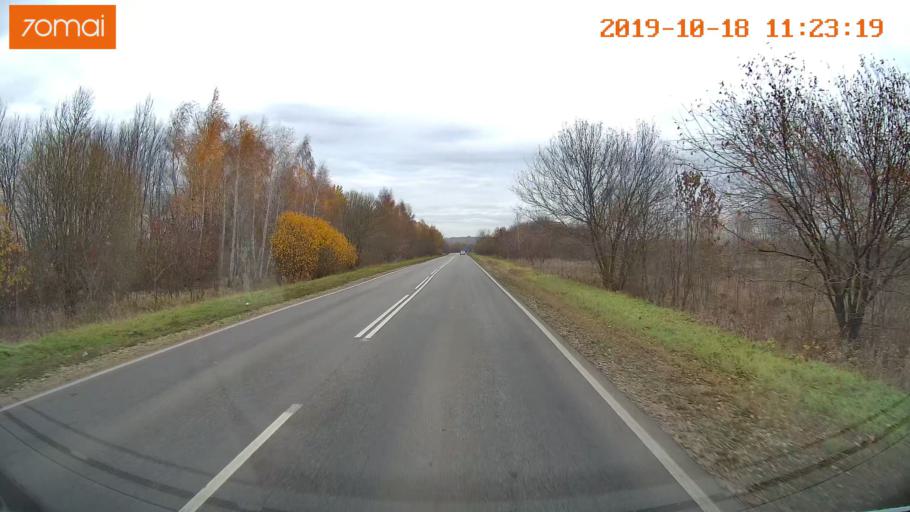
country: RU
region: Tula
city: Kimovsk
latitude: 54.1000
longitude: 38.5925
